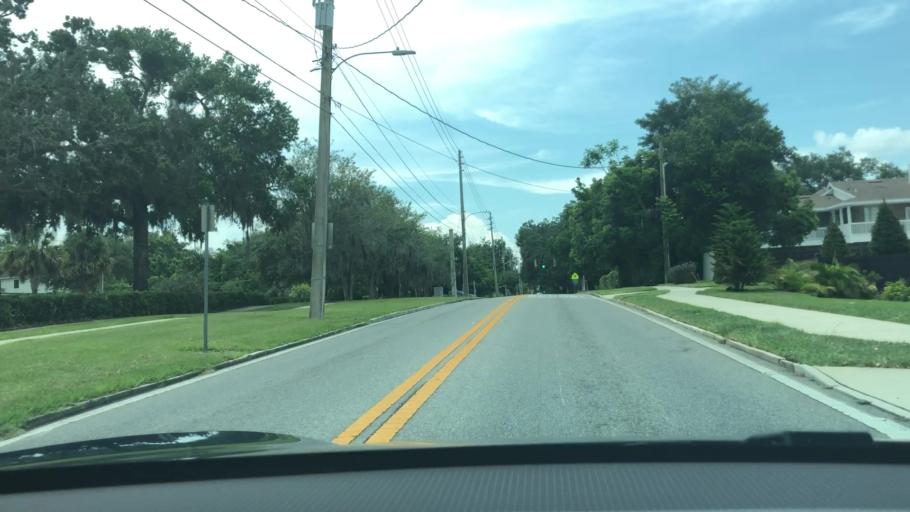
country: US
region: Florida
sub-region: Orange County
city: Orlando
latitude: 28.5203
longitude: -81.3669
